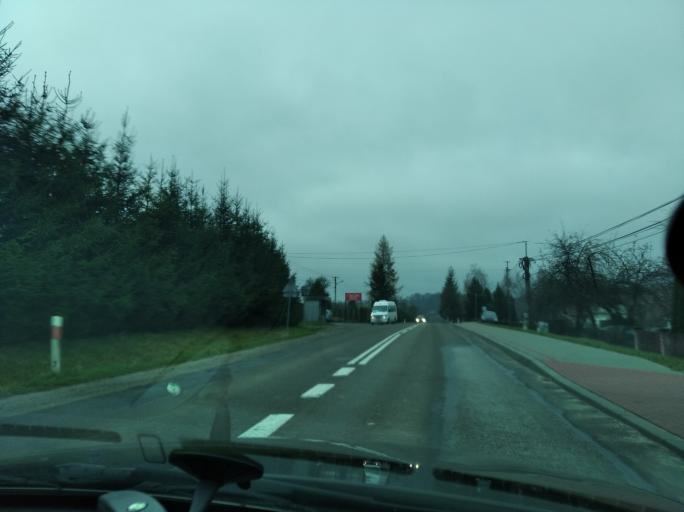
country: PL
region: Subcarpathian Voivodeship
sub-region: Powiat przeworski
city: Jawornik Polski
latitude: 49.8724
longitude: 22.2460
